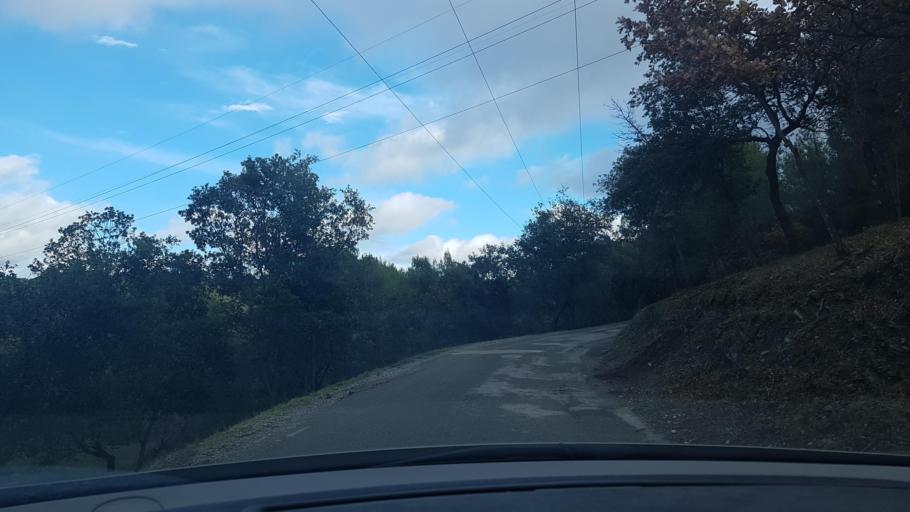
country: FR
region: Provence-Alpes-Cote d'Azur
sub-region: Departement des Bouches-du-Rhone
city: Simiane-Collongue
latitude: 43.4149
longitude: 5.4653
